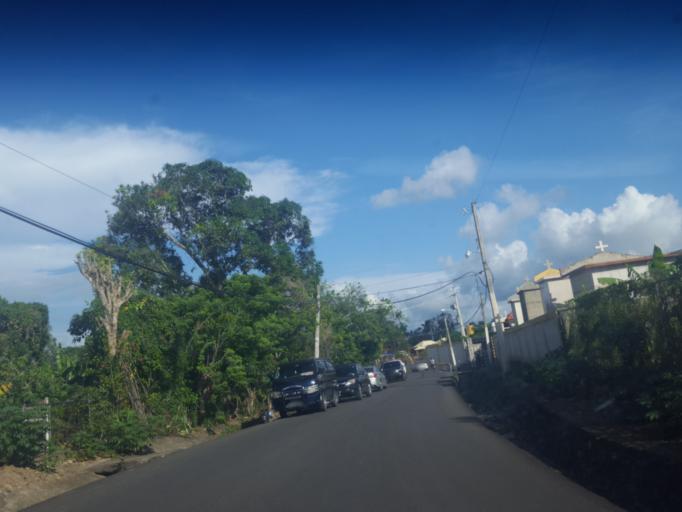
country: DO
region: La Vega
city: Rio Verde Arriba
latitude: 19.3464
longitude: -70.6225
